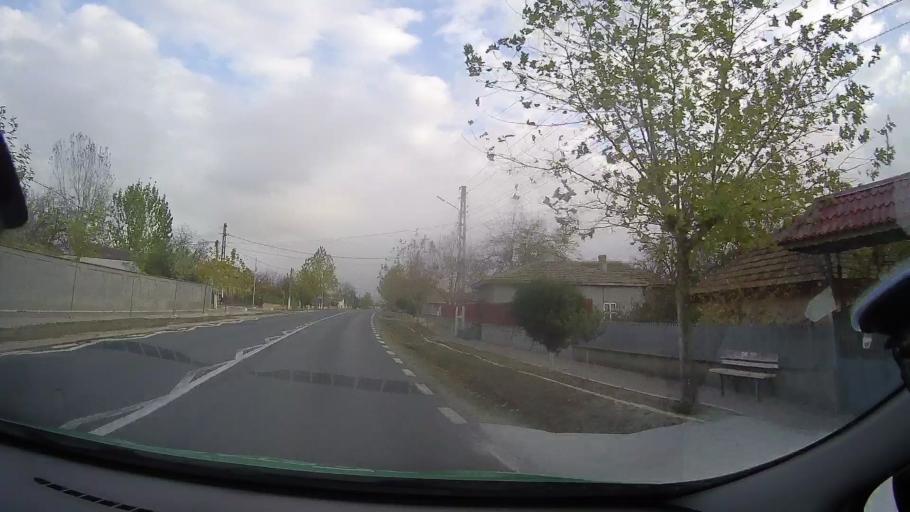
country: RO
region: Constanta
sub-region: Comuna Mircea Voda
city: Satu Nou
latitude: 44.2676
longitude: 28.2260
